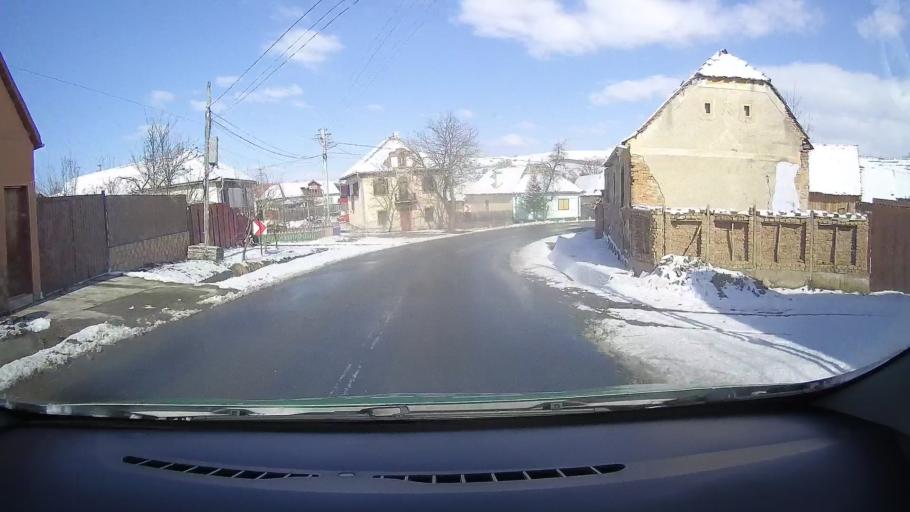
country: RO
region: Sibiu
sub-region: Comuna Barghis
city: Barghis
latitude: 45.9886
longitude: 24.4836
